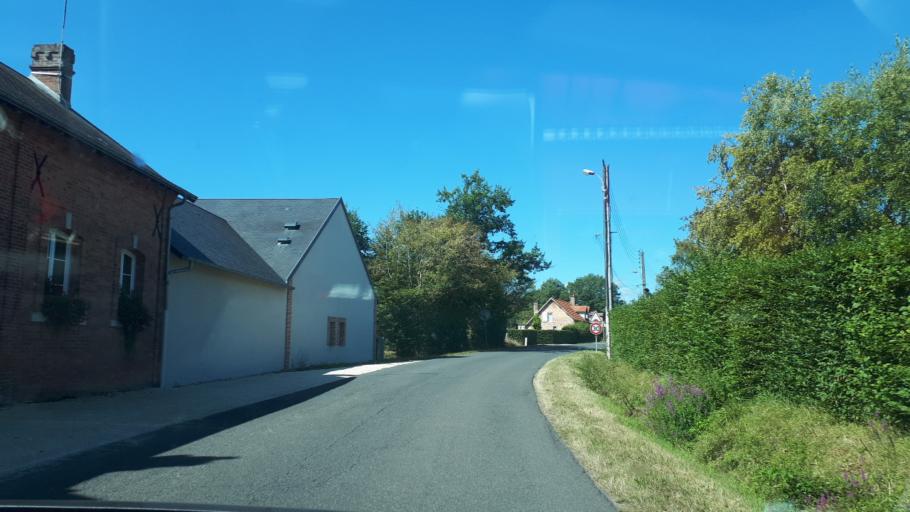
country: FR
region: Centre
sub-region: Departement du Loir-et-Cher
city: Vouzon
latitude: 47.6429
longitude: 2.1603
